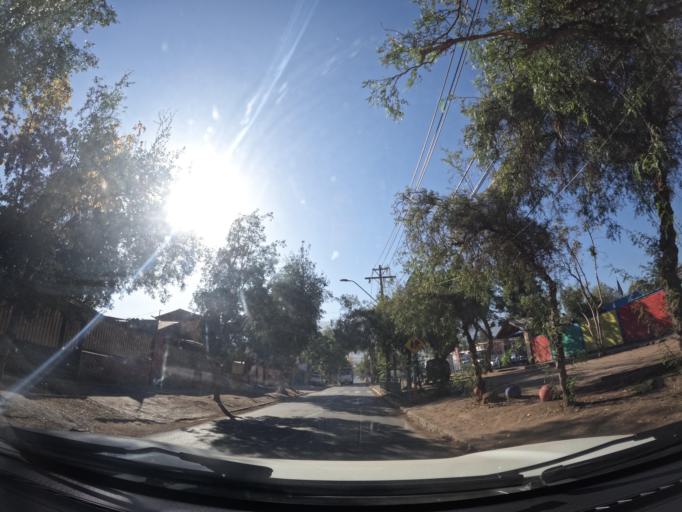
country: CL
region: Santiago Metropolitan
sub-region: Provincia de Santiago
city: Villa Presidente Frei, Nunoa, Santiago, Chile
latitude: -33.4682
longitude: -70.5657
